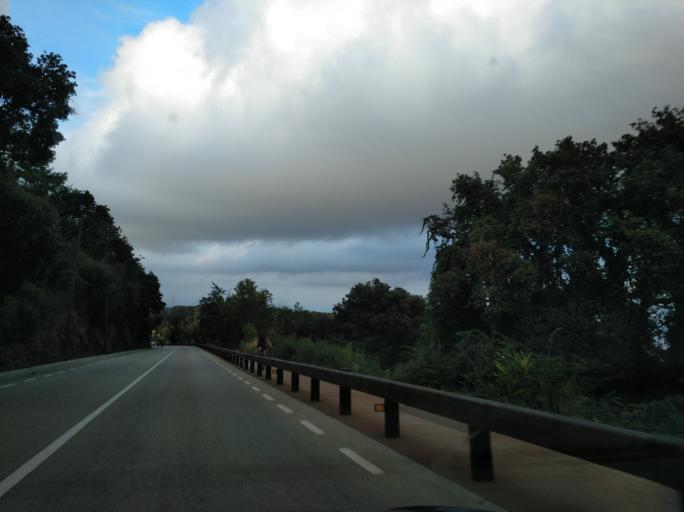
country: ES
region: Catalonia
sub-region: Provincia de Barcelona
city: Sarria-Sant Gervasi
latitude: 41.4253
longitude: 2.1226
